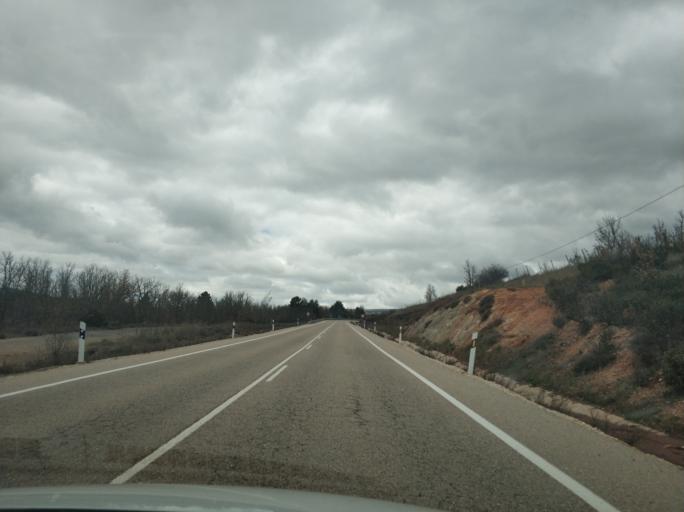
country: ES
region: Castille and Leon
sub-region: Provincia de Burgos
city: Pinilla de los Barruecos
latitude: 41.9382
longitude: -3.2862
